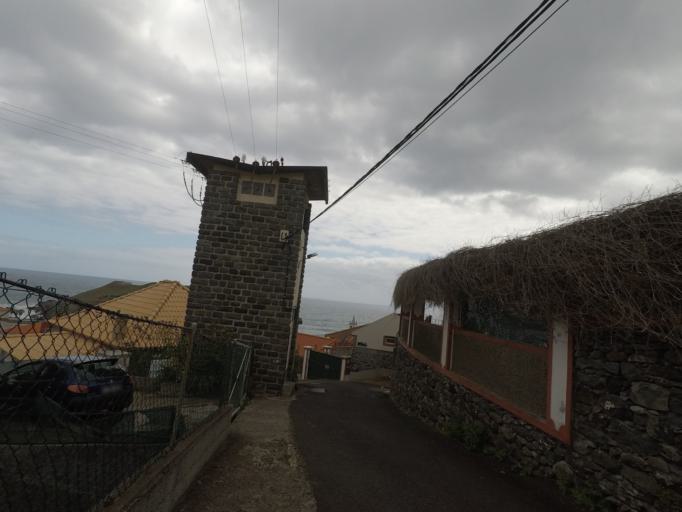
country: PT
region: Madeira
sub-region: Santana
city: Santana
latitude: 32.7715
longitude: -16.8298
